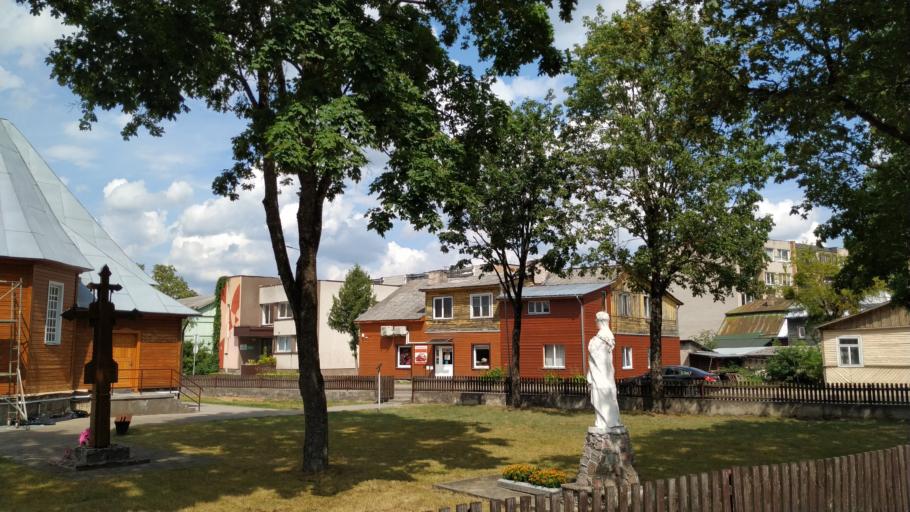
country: LT
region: Alytaus apskritis
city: Varena
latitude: 54.2095
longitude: 24.5725
